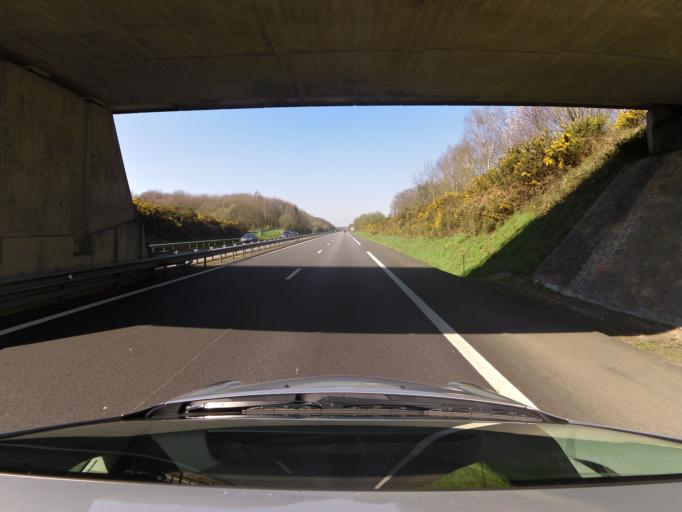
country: FR
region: Brittany
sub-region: Departement du Morbihan
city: Ploermel
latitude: 47.9186
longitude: -2.3704
